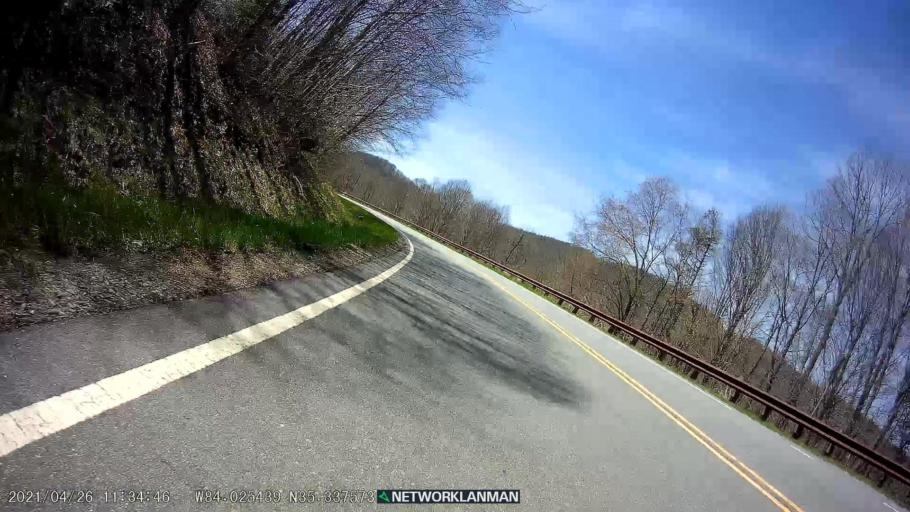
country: US
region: North Carolina
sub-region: Graham County
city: Robbinsville
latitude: 35.3377
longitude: -84.0249
